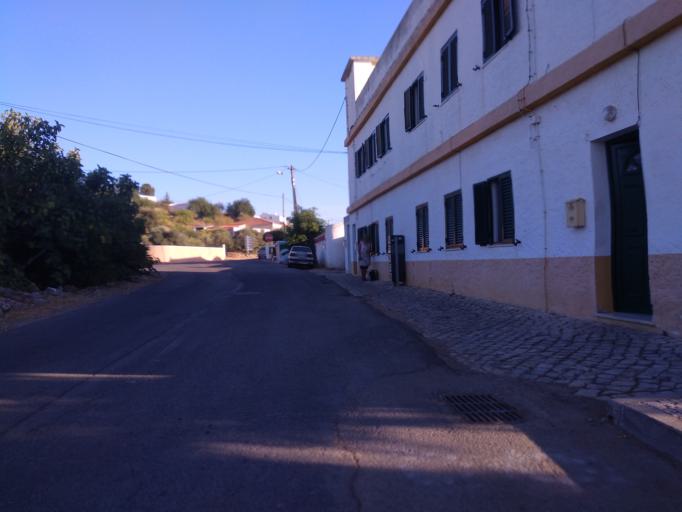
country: PT
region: Faro
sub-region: Sao Bras de Alportel
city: Sao Bras de Alportel
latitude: 37.1663
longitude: -7.8925
